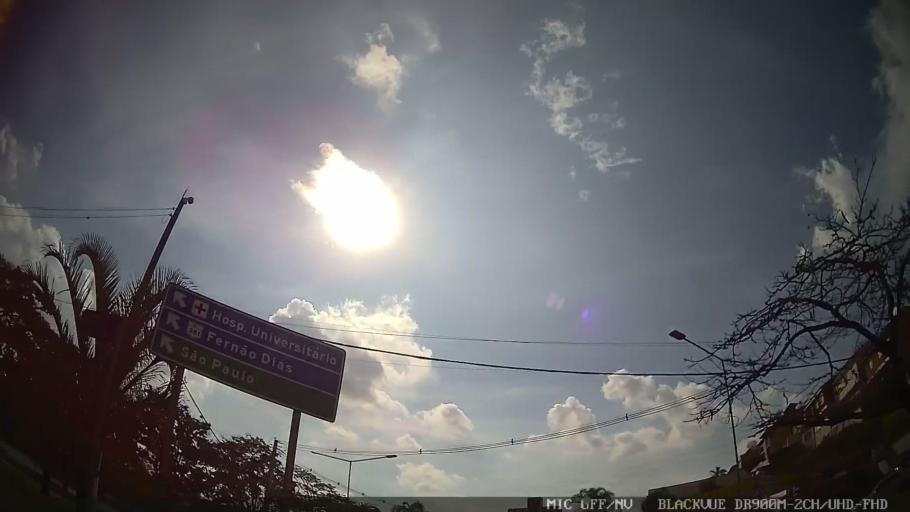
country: BR
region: Sao Paulo
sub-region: Braganca Paulista
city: Braganca Paulista
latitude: -22.9694
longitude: -46.5367
